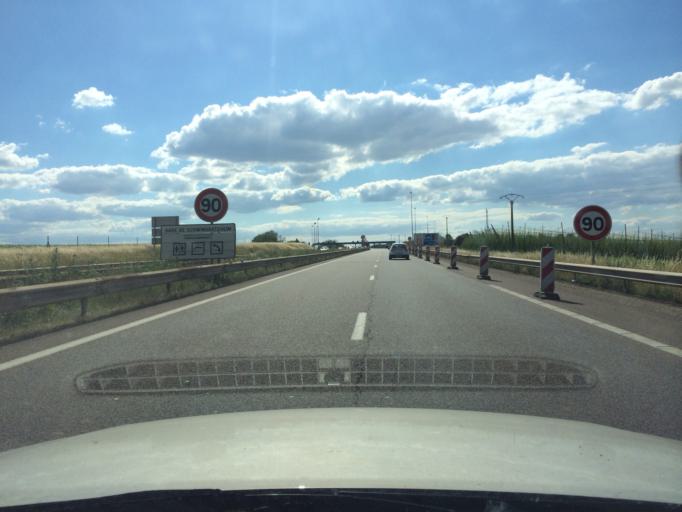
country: FR
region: Alsace
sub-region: Departement du Bas-Rhin
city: Schwindratzheim
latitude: 48.7702
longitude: 7.6098
